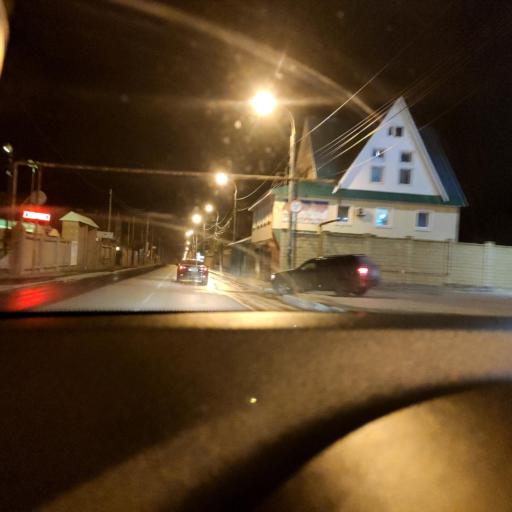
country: RU
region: Samara
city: Samara
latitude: 53.2647
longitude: 50.2105
